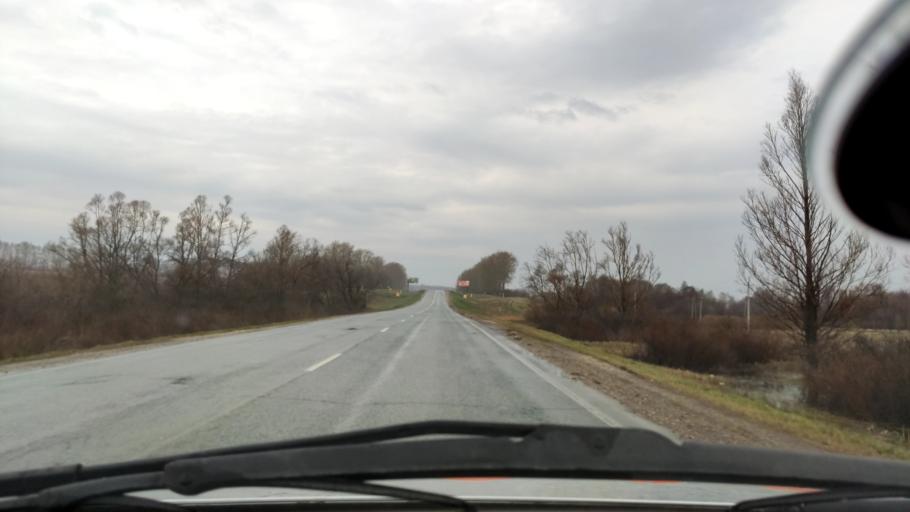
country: RU
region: Bashkortostan
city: Sterlitamak
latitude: 53.7337
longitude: 55.9426
